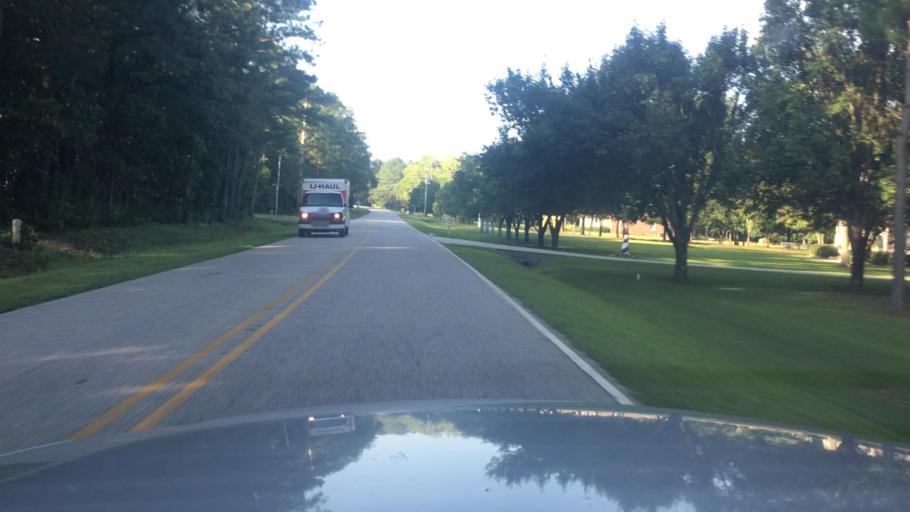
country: US
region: North Carolina
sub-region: Cumberland County
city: Spring Lake
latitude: 35.2226
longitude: -78.8922
